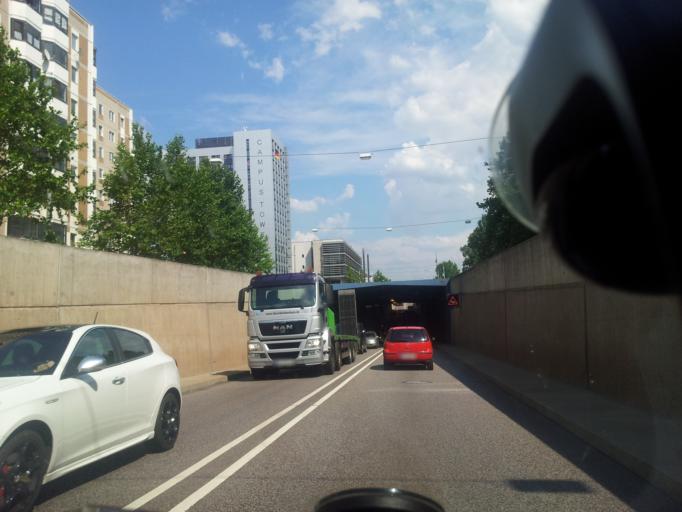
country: DE
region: Saxony-Anhalt
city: Neue Neustadt
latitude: 52.1391
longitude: 11.6380
